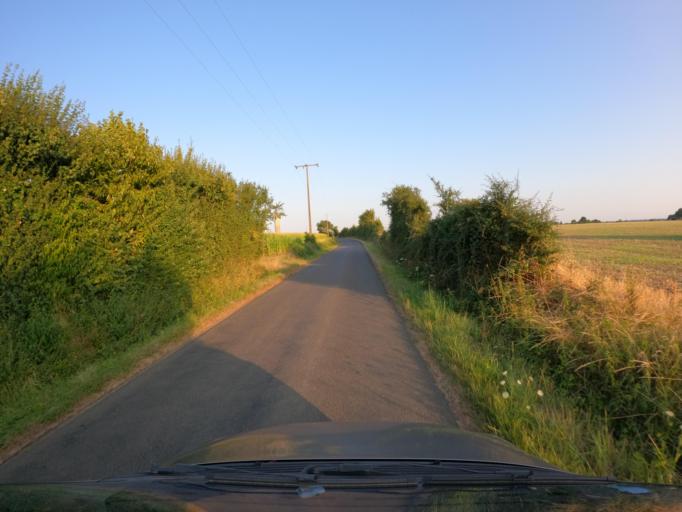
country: FR
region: Pays de la Loire
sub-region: Departement de la Sarthe
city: Parce-sur-Sarthe
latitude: 47.8801
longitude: -0.2204
